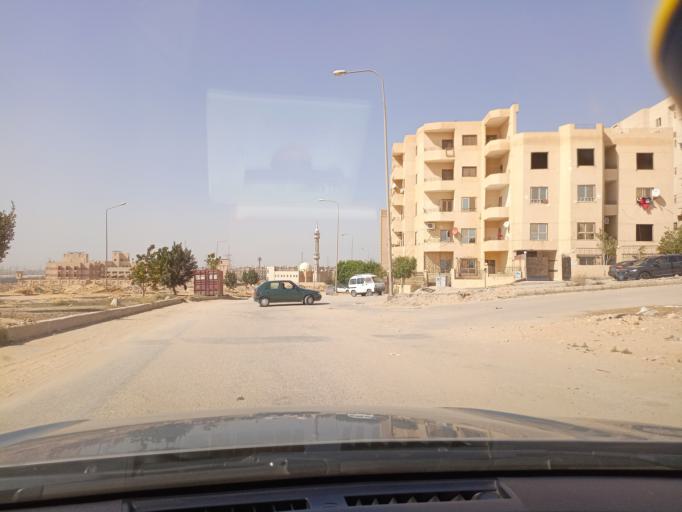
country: EG
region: Muhafazat al Qalyubiyah
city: Al Khankah
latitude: 30.2248
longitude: 31.4394
